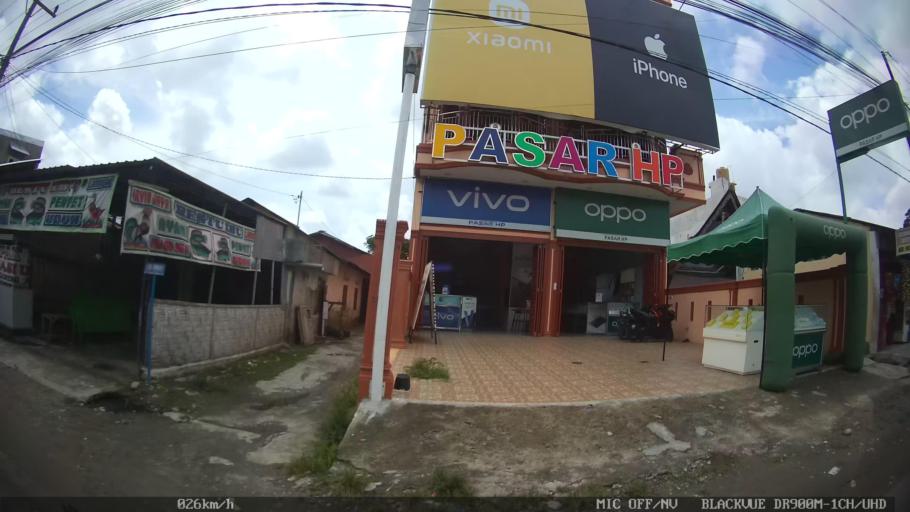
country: ID
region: North Sumatra
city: Medan
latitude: 3.6204
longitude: 98.7332
